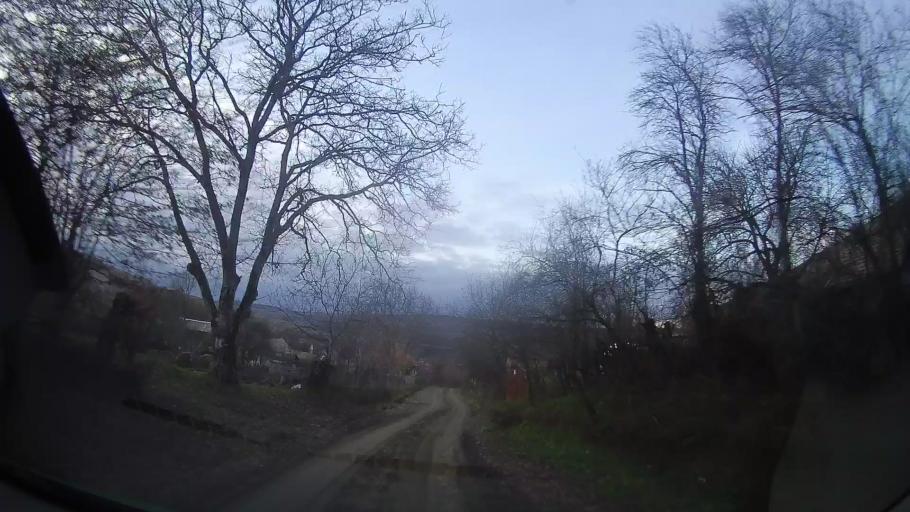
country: RO
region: Cluj
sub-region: Comuna Palatca
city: Palatca
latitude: 46.8621
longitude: 24.0235
